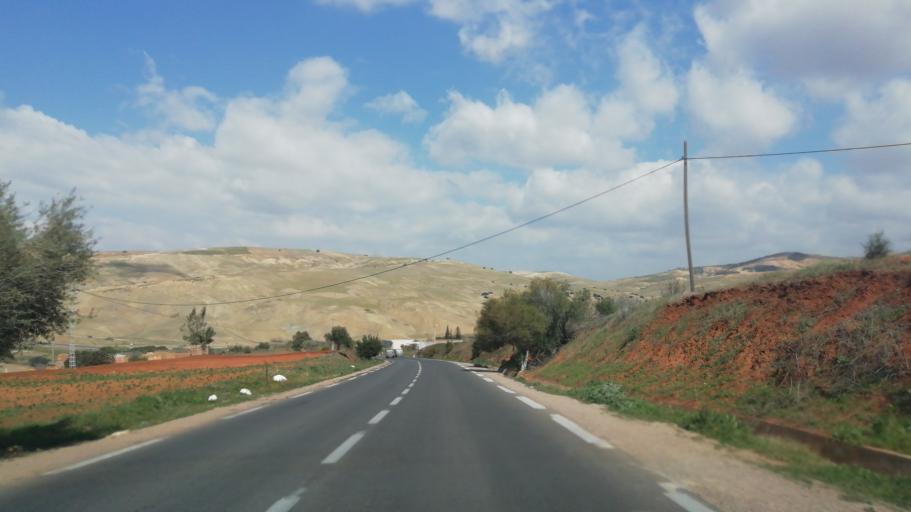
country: DZ
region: Mascara
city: Mascara
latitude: 35.5358
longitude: 0.1125
